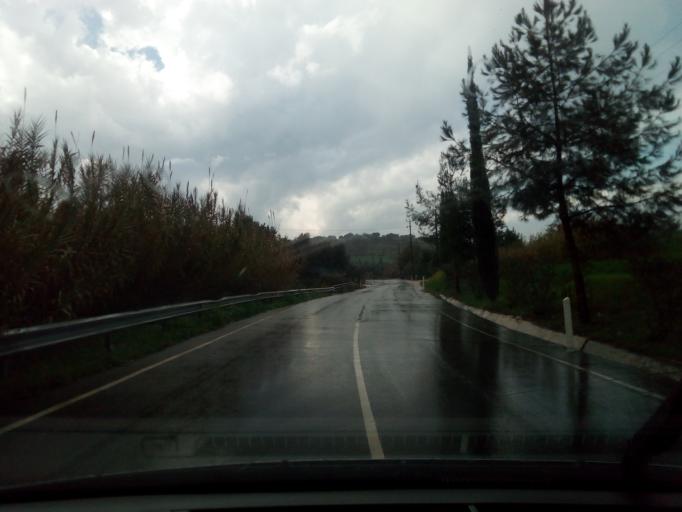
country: CY
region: Pafos
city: Polis
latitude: 35.0034
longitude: 32.4642
